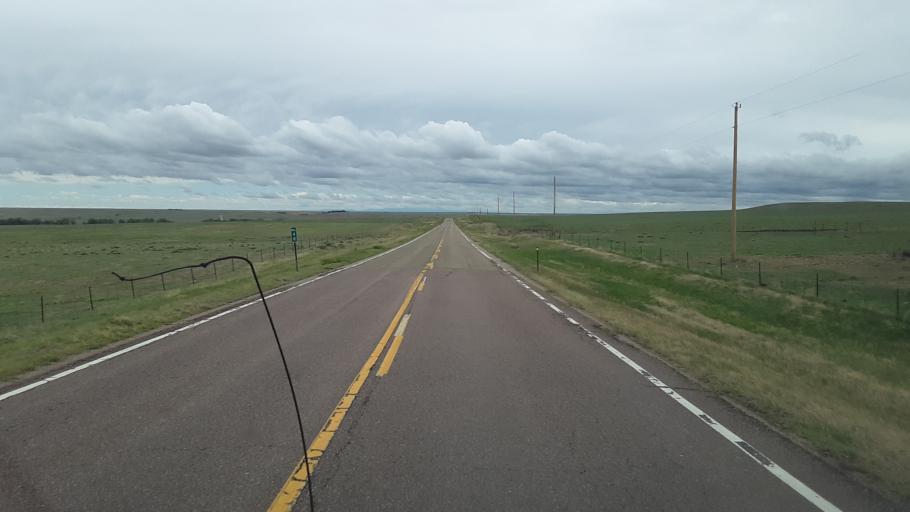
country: US
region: Colorado
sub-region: Lincoln County
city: Limon
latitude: 38.8379
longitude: -103.8143
